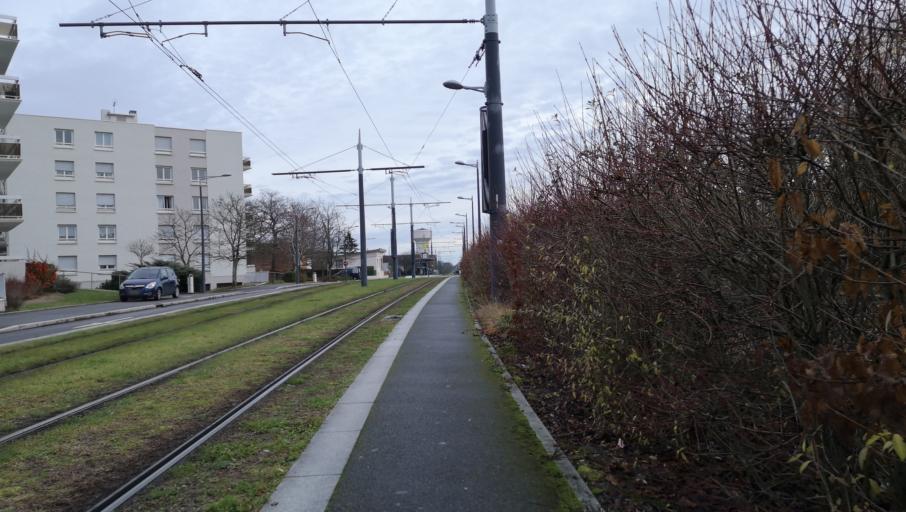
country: FR
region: Centre
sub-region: Departement du Loiret
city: Saint-Jean-de-Braye
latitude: 47.9091
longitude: 1.9570
